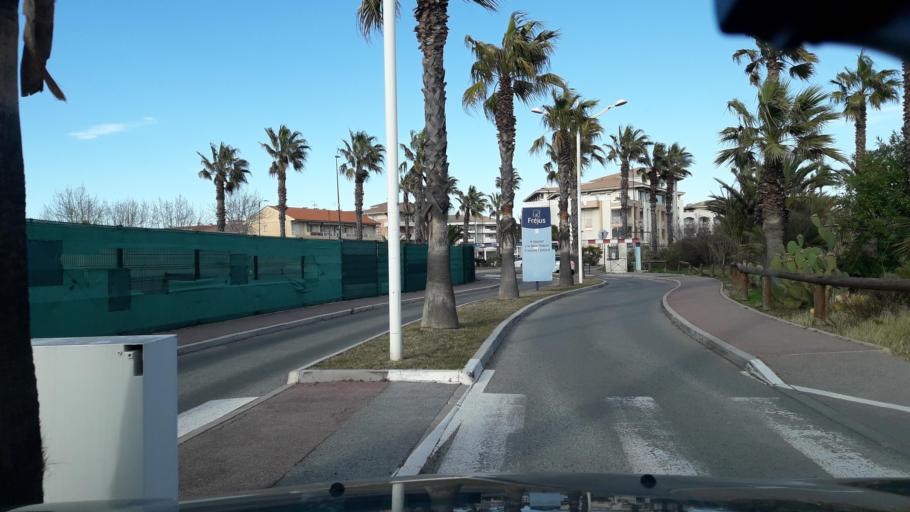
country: FR
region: Provence-Alpes-Cote d'Azur
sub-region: Departement du Var
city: Frejus
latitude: 43.4187
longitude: 6.7452
